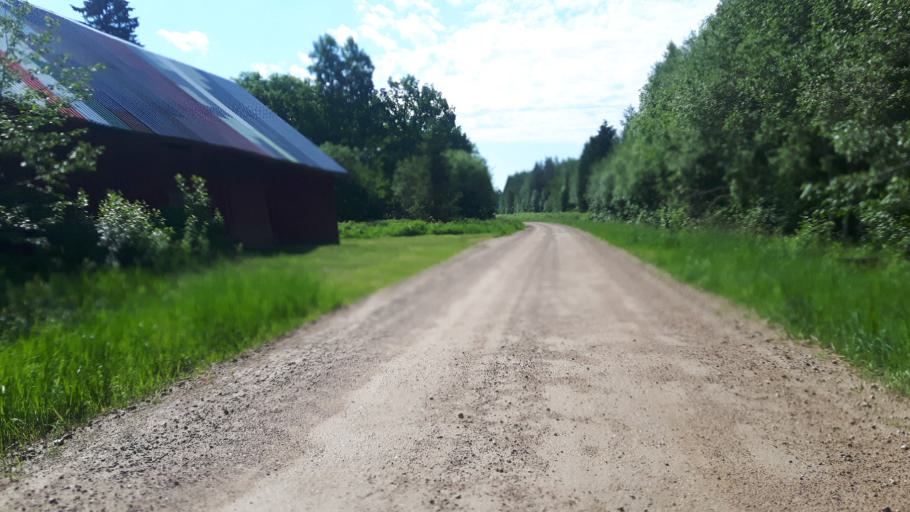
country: EE
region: Paernumaa
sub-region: Vaendra vald (alev)
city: Vandra
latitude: 58.6967
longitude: 25.0309
